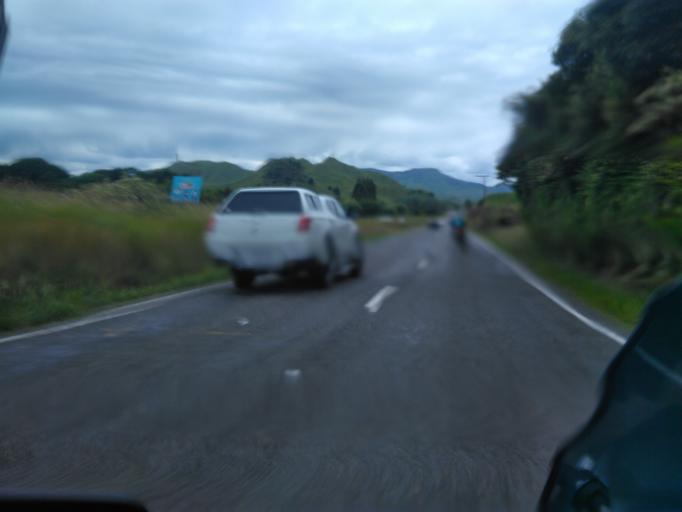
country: NZ
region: Bay of Plenty
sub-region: Opotiki District
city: Opotiki
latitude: -38.3629
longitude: 177.4949
